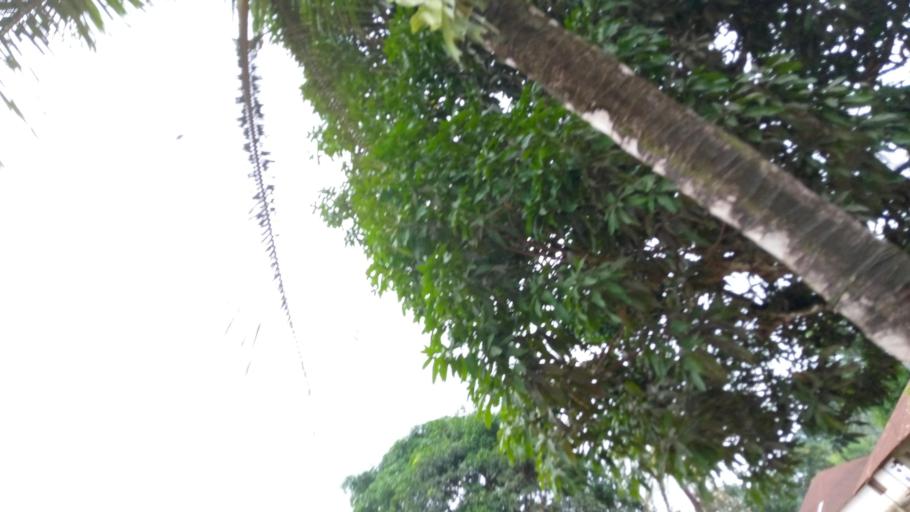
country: SL
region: Southern Province
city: Tongole
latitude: 7.4329
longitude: -11.8430
